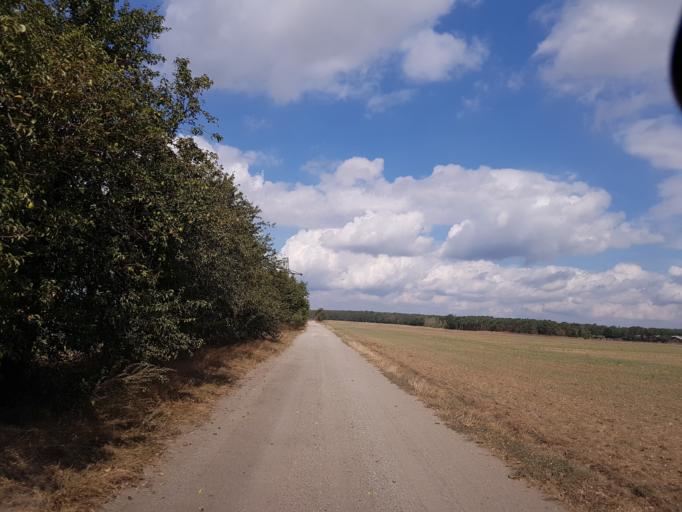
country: DE
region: Brandenburg
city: Finsterwalde
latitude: 51.6259
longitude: 13.7548
